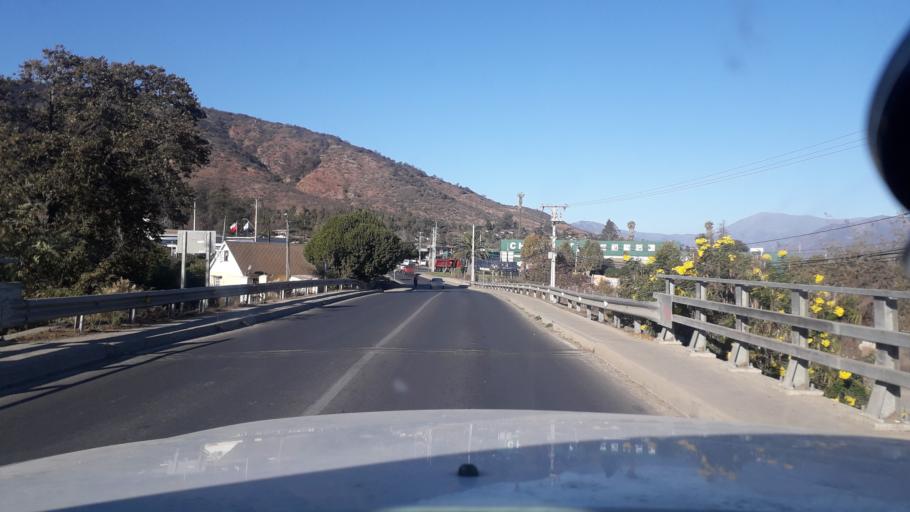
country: CL
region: Valparaiso
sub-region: Provincia de Marga Marga
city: Limache
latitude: -32.9823
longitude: -71.2774
